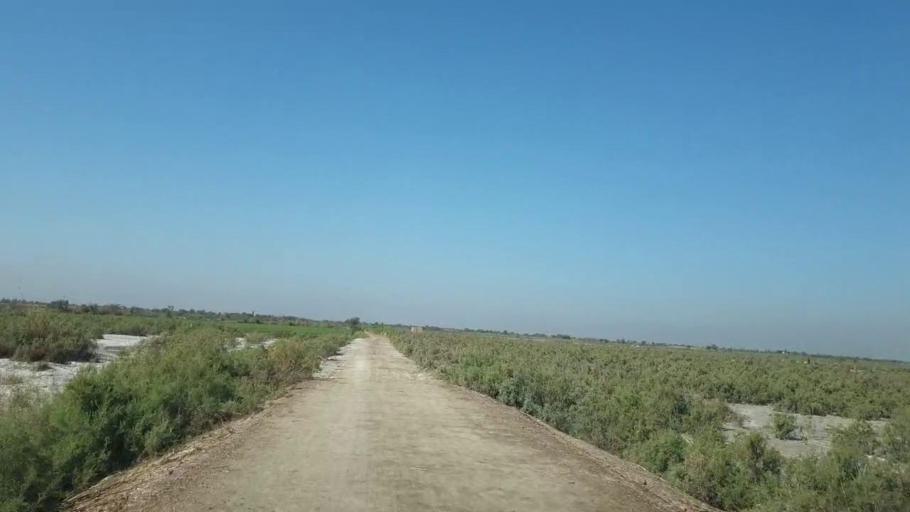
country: PK
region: Sindh
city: Mirpur Khas
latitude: 25.6217
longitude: 69.0233
